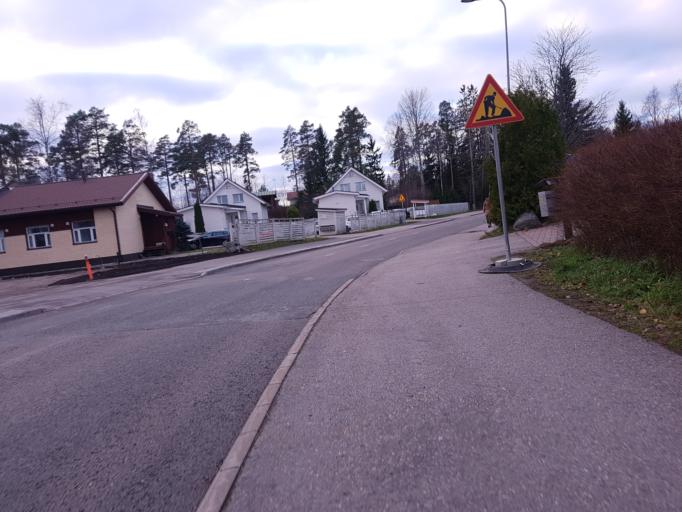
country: FI
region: Uusimaa
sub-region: Helsinki
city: Helsinki
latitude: 60.2793
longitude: 24.9125
